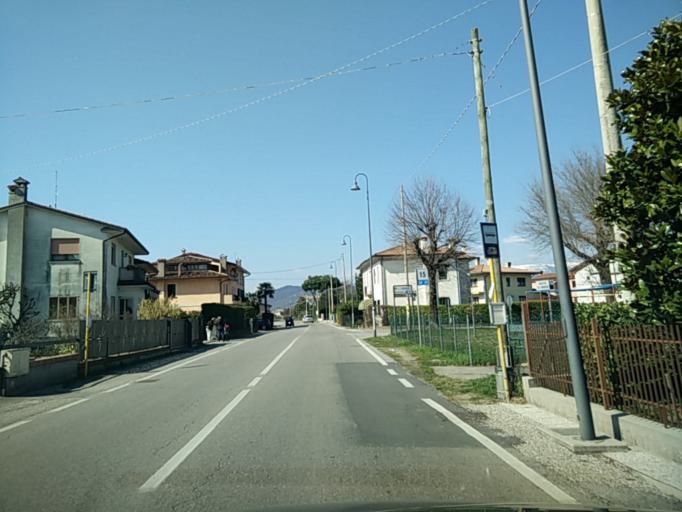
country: IT
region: Veneto
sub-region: Provincia di Treviso
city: Ciano
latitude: 45.8258
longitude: 12.0461
